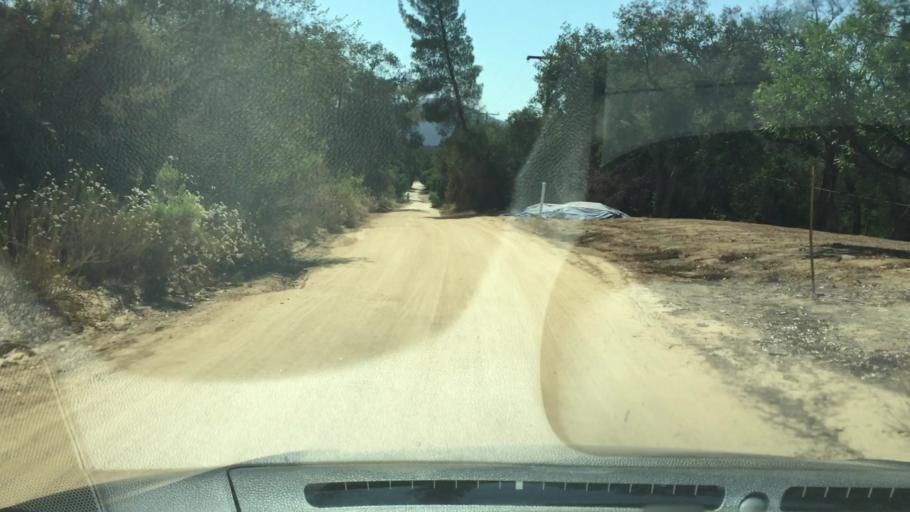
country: US
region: California
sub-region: San Diego County
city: Alpine
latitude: 32.7538
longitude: -116.7509
